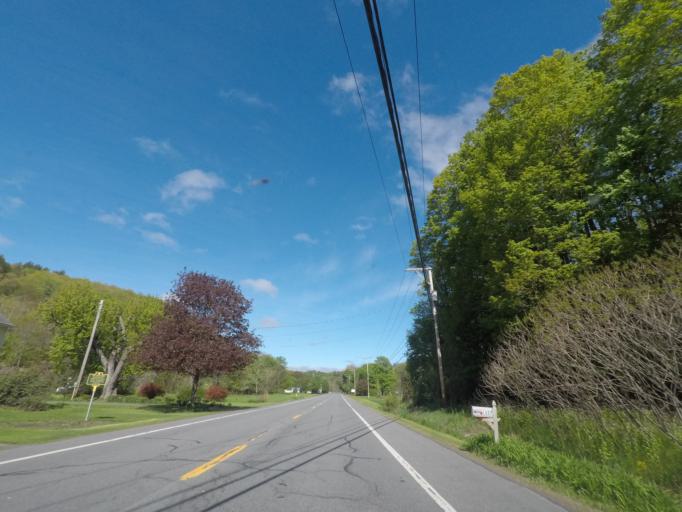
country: US
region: New York
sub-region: Albany County
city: Ravena
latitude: 42.4728
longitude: -73.8984
